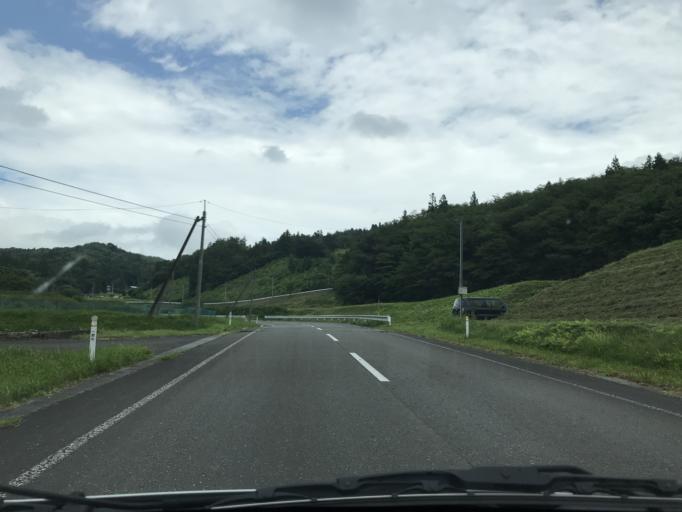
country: JP
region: Iwate
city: Mizusawa
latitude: 39.0524
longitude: 141.3731
